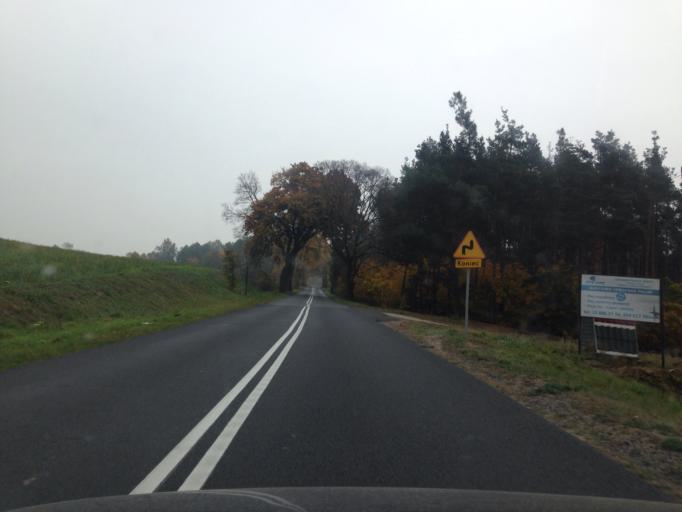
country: PL
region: Kujawsko-Pomorskie
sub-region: Powiat brodnicki
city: Bartniczka
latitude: 53.2455
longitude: 19.6410
